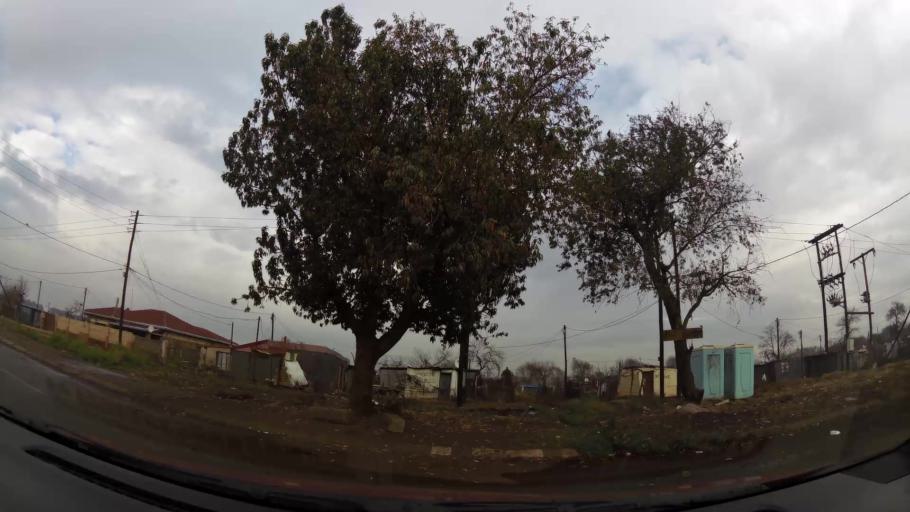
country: ZA
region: Gauteng
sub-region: City of Johannesburg Metropolitan Municipality
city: Soweto
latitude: -26.2834
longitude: 27.8363
